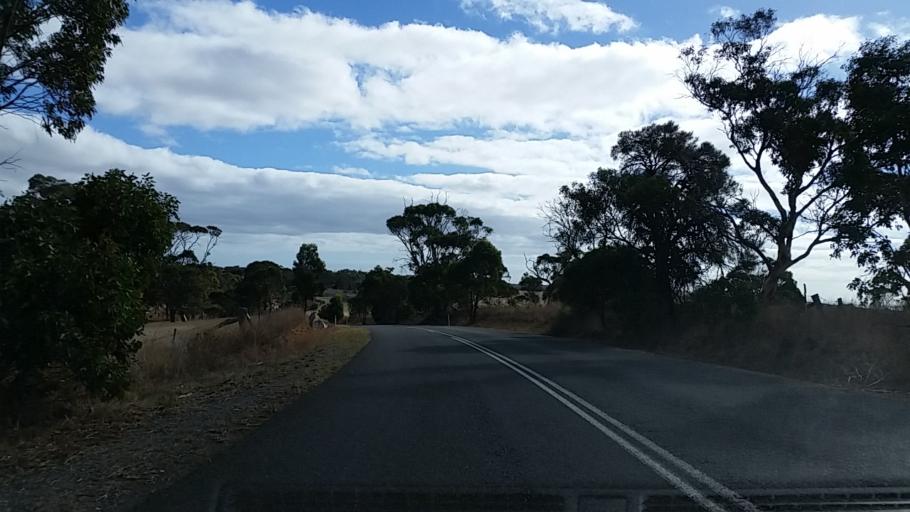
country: AU
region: South Australia
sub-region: Yankalilla
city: Normanville
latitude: -35.4107
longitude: 138.3936
